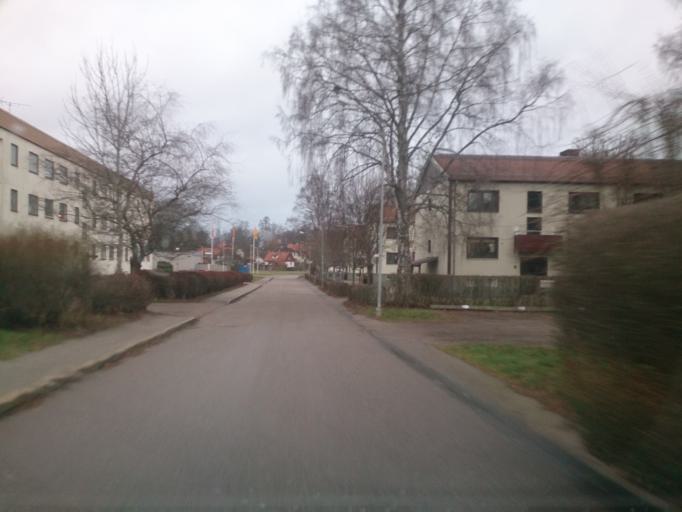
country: SE
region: OEstergoetland
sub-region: Atvidabergs Kommun
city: Atvidaberg
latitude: 58.1941
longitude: 16.0031
